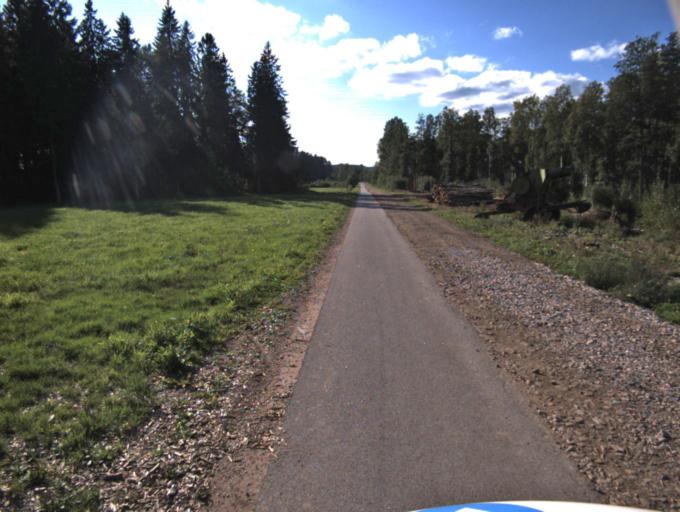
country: SE
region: Vaestra Goetaland
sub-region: Boras Kommun
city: Dalsjofors
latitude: 57.8248
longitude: 13.1706
